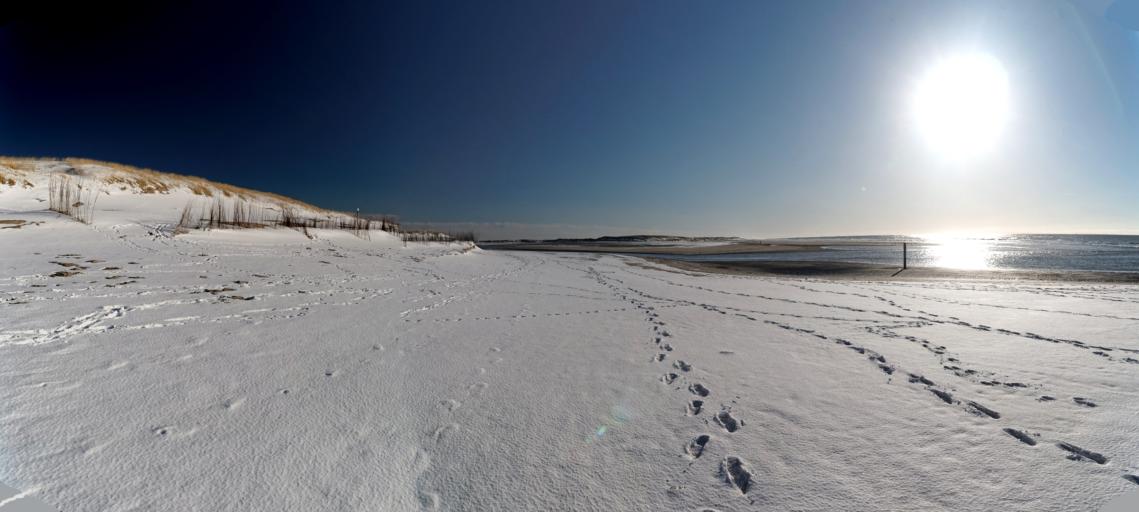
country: NL
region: North Holland
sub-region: Gemeente Texel
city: Den Burg
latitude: 53.1431
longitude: 4.8014
